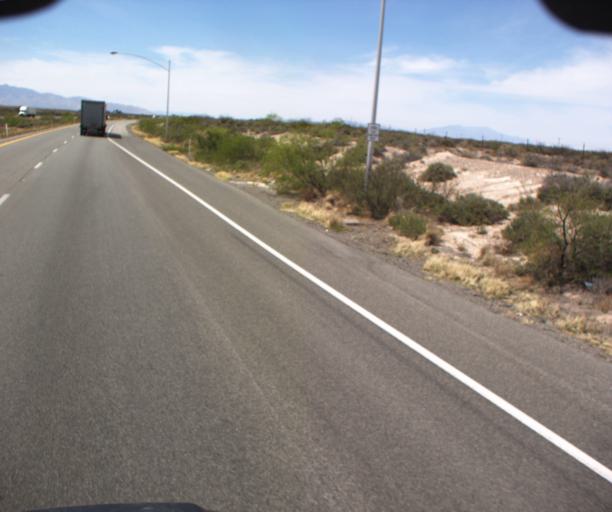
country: US
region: New Mexico
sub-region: Hidalgo County
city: Lordsburg
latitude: 32.2575
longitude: -109.1990
